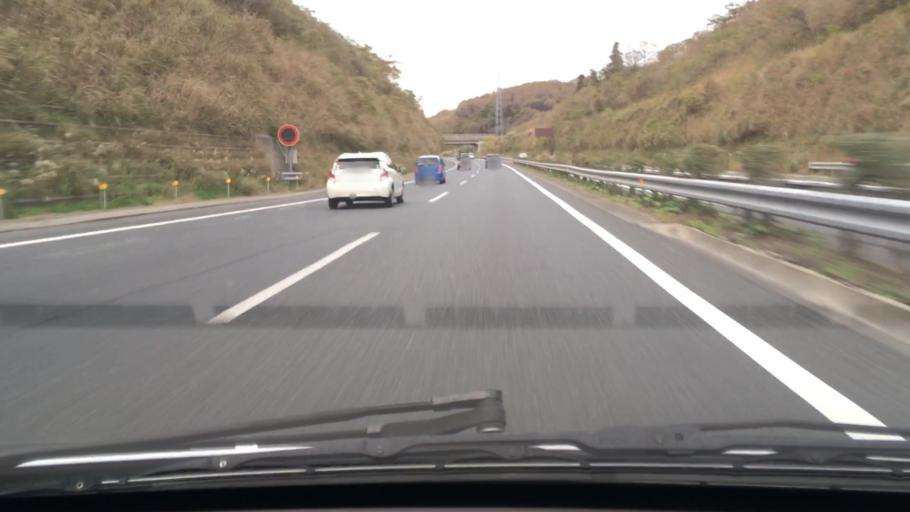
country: JP
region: Chiba
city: Kimitsu
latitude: 35.3229
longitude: 139.9452
